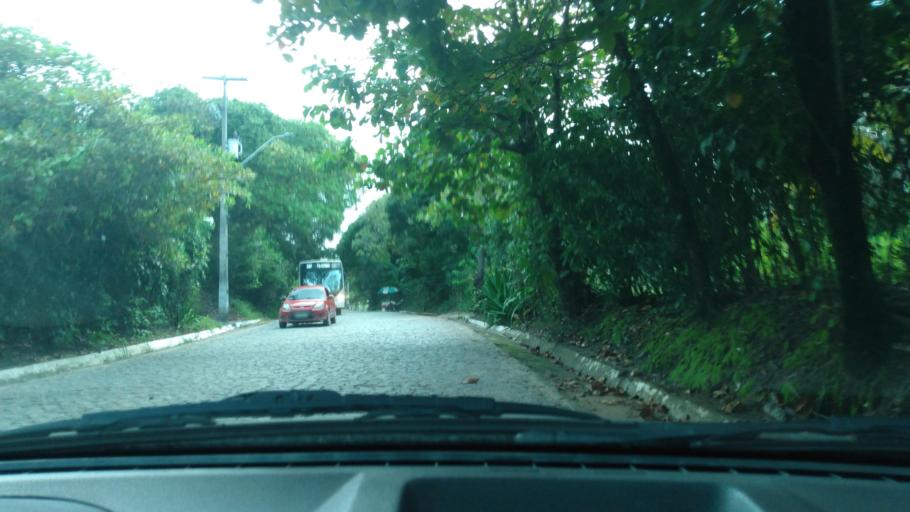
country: BR
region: Pernambuco
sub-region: Cabo De Santo Agostinho
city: Cabo
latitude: -8.3464
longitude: -34.9551
